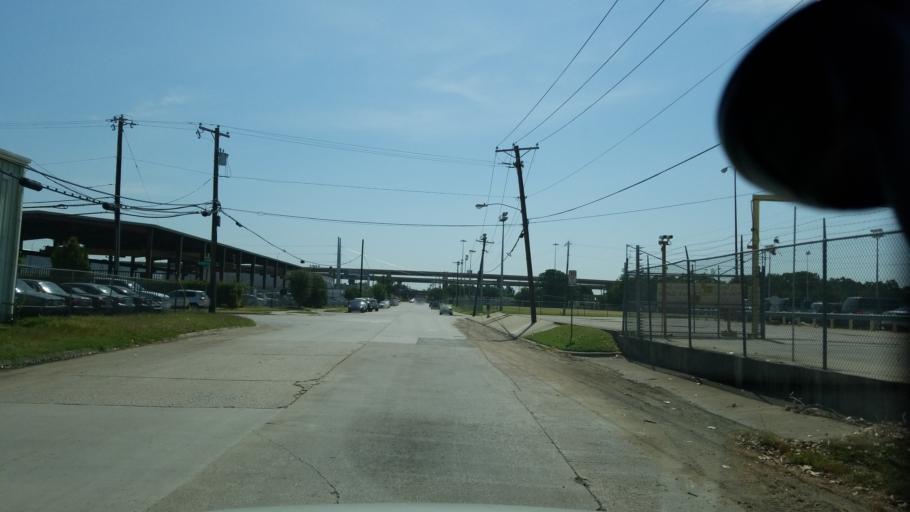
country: US
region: Texas
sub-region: Dallas County
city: Farmers Branch
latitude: 32.9004
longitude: -96.9029
